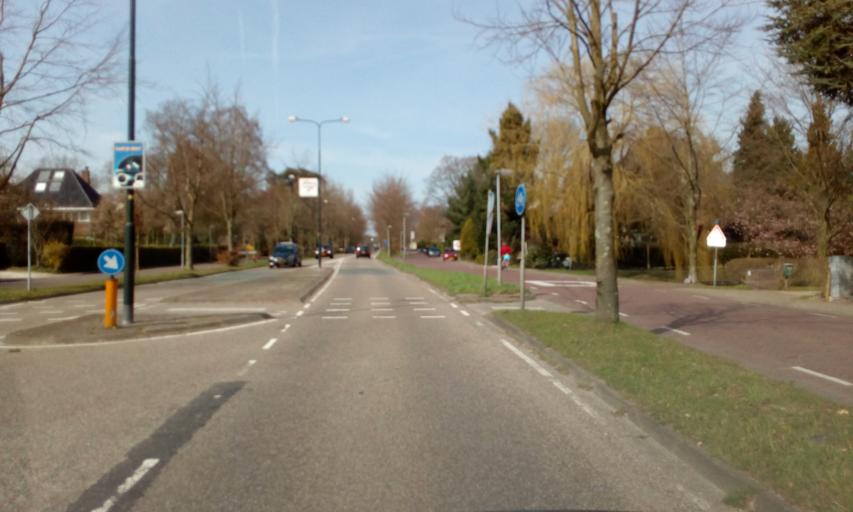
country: NL
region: North Holland
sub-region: Gemeente Naarden
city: Naarden
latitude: 52.2846
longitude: 5.1776
